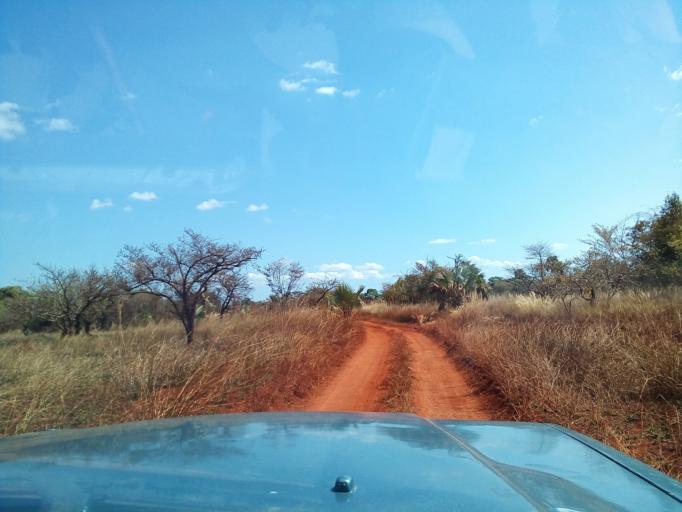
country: MG
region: Boeny
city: Mahajanga
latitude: -15.9907
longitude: 46.0209
